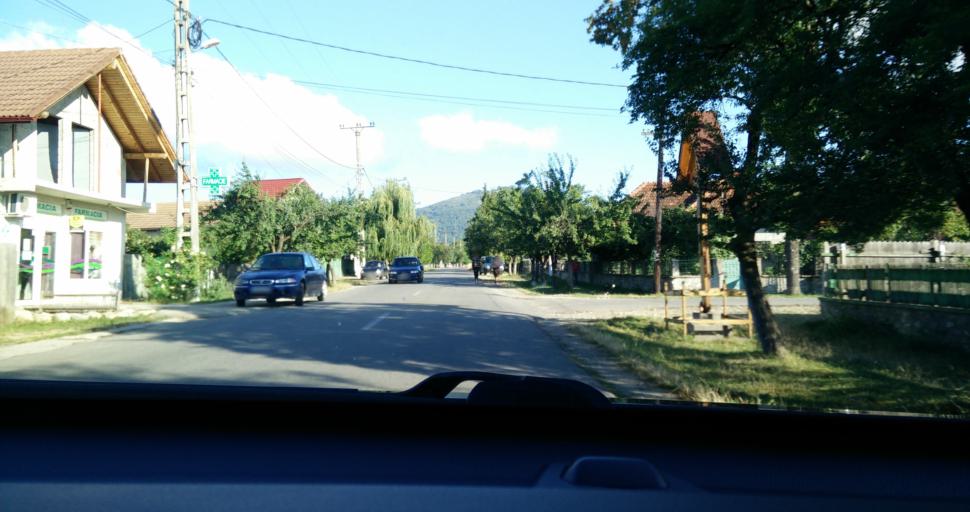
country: RO
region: Gorj
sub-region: Comuna Polovragi
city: Polovragi
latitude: 45.1729
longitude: 23.8023
